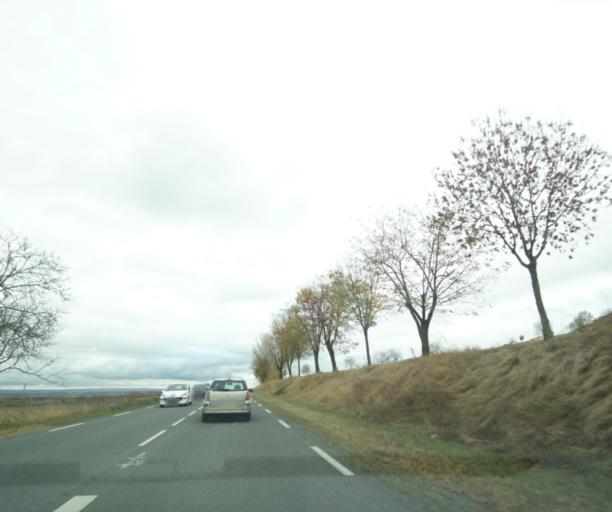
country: FR
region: Auvergne
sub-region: Departement du Puy-de-Dome
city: Pont-du-Chateau
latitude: 45.8013
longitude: 3.2264
